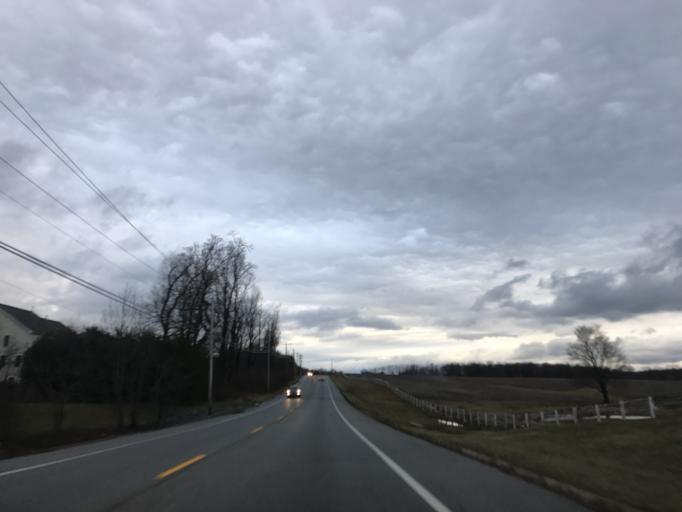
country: US
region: Maryland
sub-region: Harford County
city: Bel Air South
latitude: 39.5266
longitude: -76.2894
